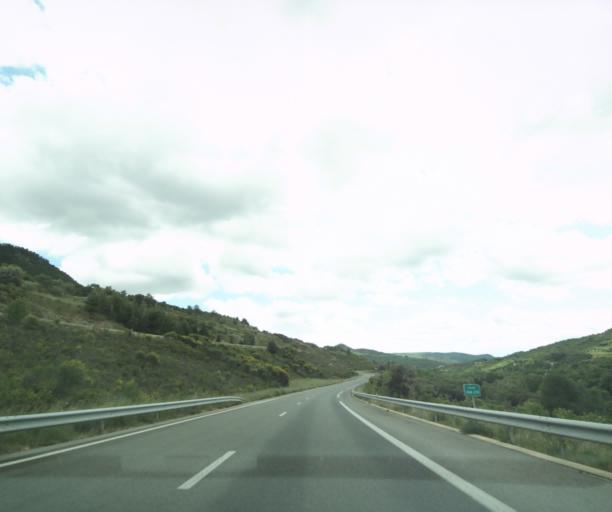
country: FR
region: Languedoc-Roussillon
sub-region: Departement de l'Herault
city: Lodeve
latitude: 43.7834
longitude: 3.3283
